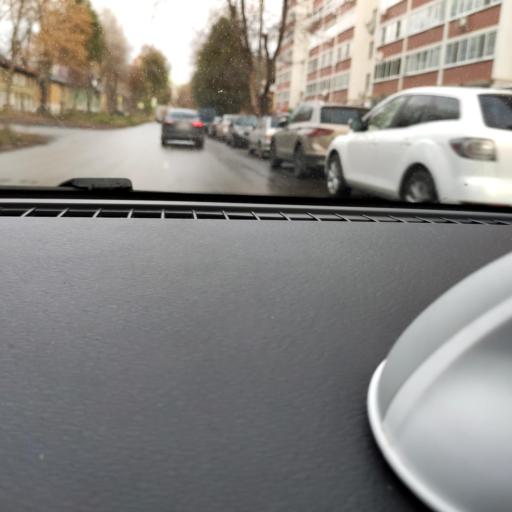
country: RU
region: Samara
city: Samara
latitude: 53.2290
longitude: 50.2640
